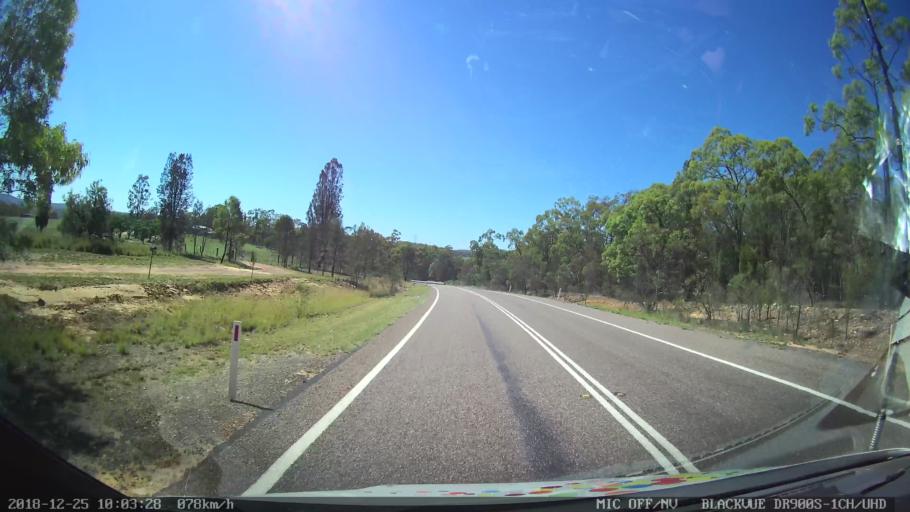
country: AU
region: New South Wales
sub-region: Upper Hunter Shire
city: Merriwa
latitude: -32.2290
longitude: 150.4709
